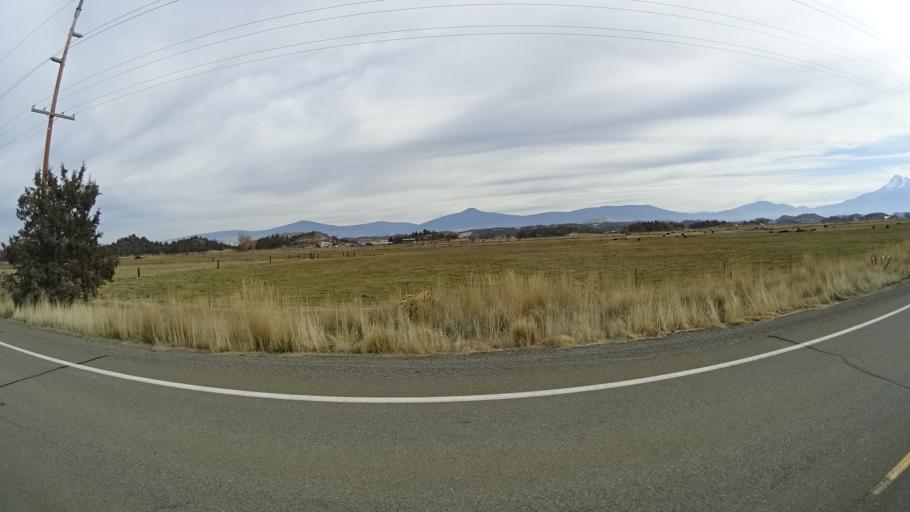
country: US
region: California
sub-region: Siskiyou County
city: Montague
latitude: 41.6692
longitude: -122.5235
